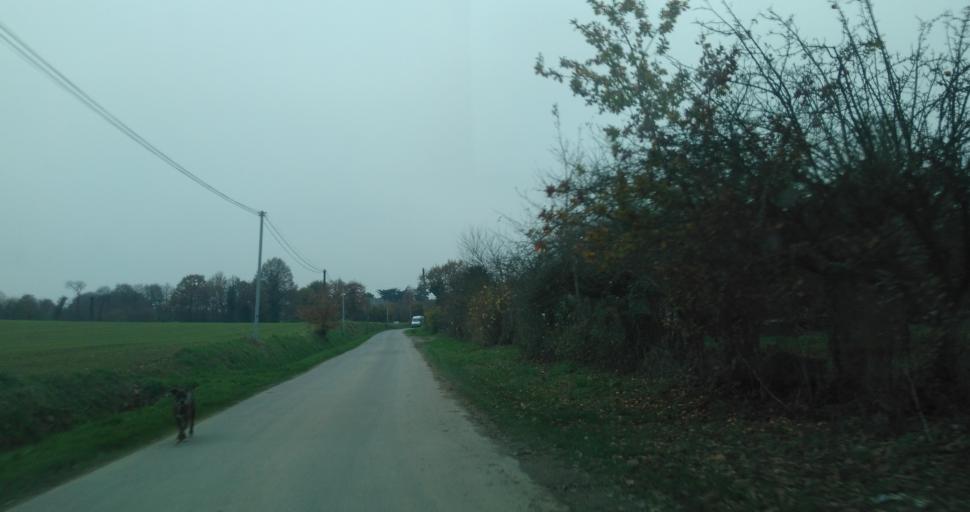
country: FR
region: Brittany
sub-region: Departement d'Ille-et-Vilaine
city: Iffendic
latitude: 48.0942
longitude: -2.0935
